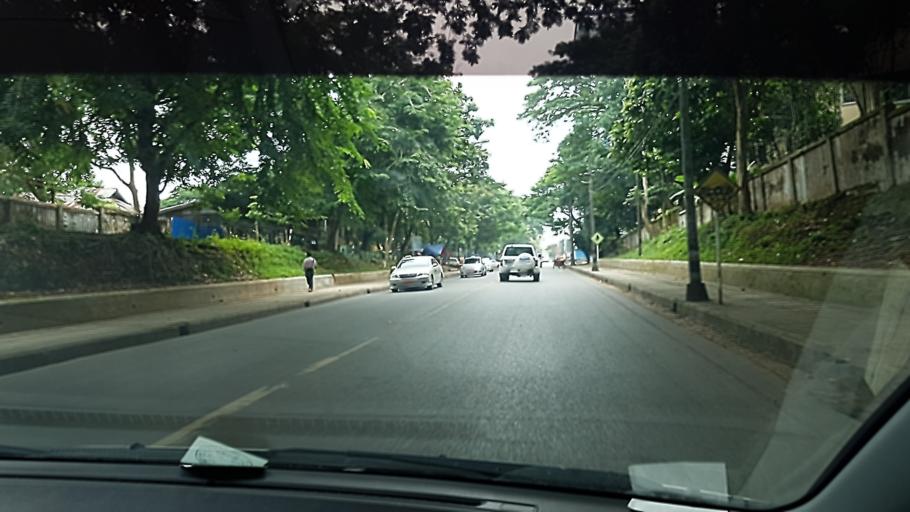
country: MM
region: Yangon
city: Yangon
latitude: 16.7899
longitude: 96.1298
